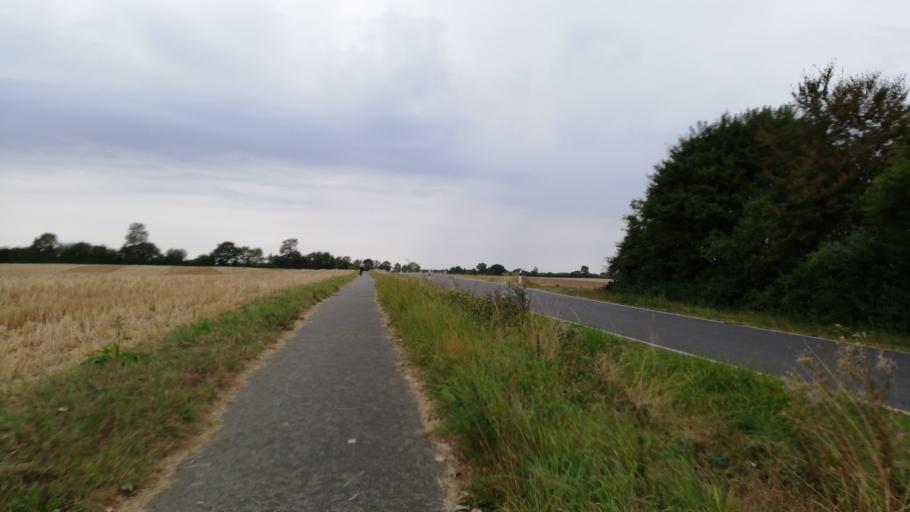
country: DE
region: Schleswig-Holstein
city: Steinbergkirche
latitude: 54.7616
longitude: 9.7642
